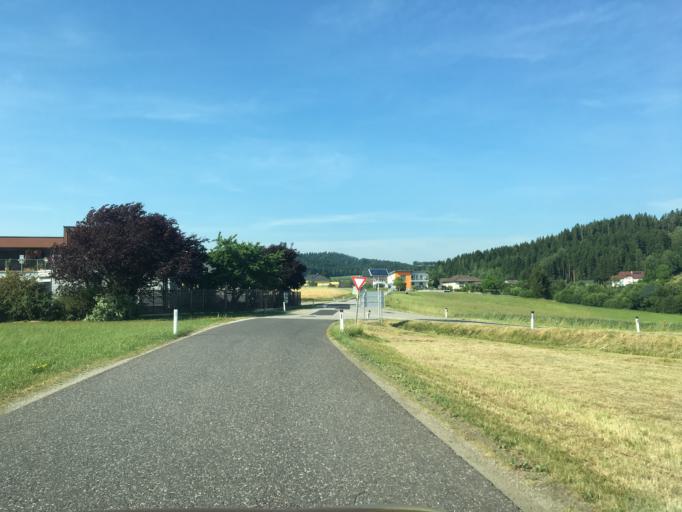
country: AT
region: Upper Austria
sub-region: Politischer Bezirk Urfahr-Umgebung
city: Herzogsdorf
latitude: 48.4228
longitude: 14.1583
